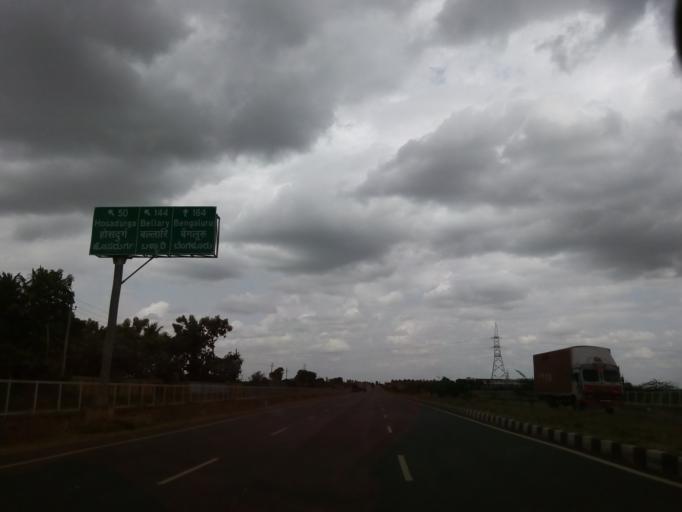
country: IN
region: Karnataka
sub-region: Chitradurga
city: Hiriyur
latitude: 13.9845
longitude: 76.5961
